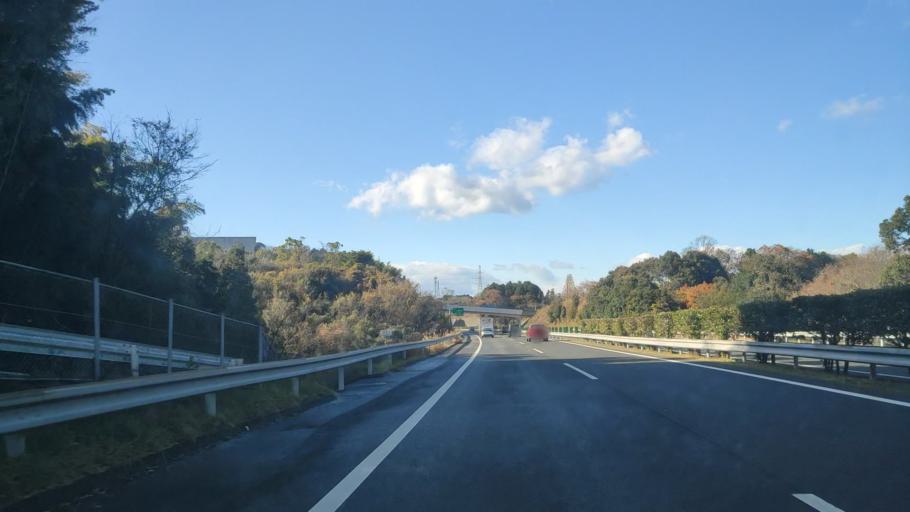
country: JP
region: Ehime
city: Saijo
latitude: 33.9105
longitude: 133.2476
